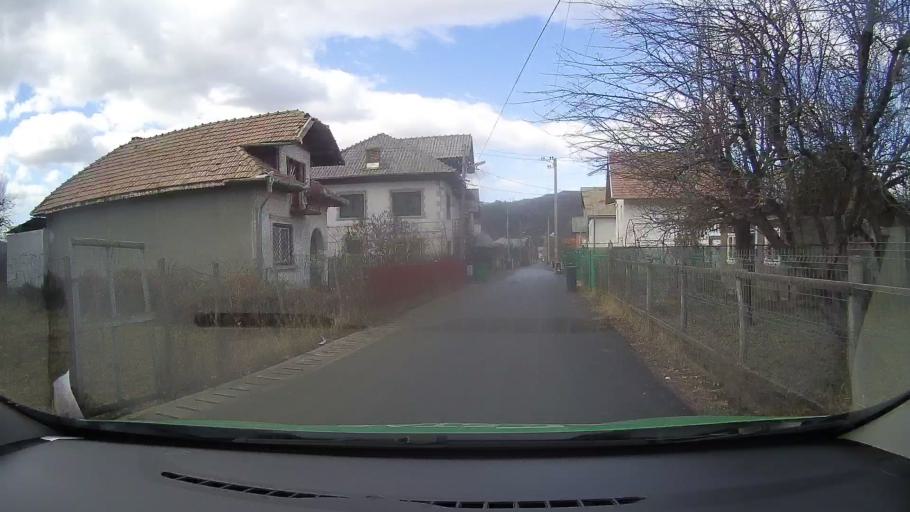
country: RO
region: Dambovita
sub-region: Comuna Buciumeni
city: Buciumeni
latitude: 45.1523
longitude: 25.4555
